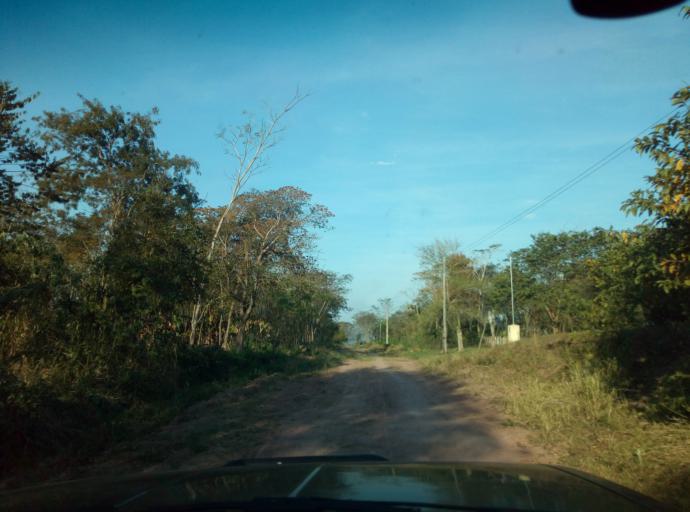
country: PY
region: Caaguazu
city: Doctor Cecilio Baez
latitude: -25.2000
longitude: -56.1333
